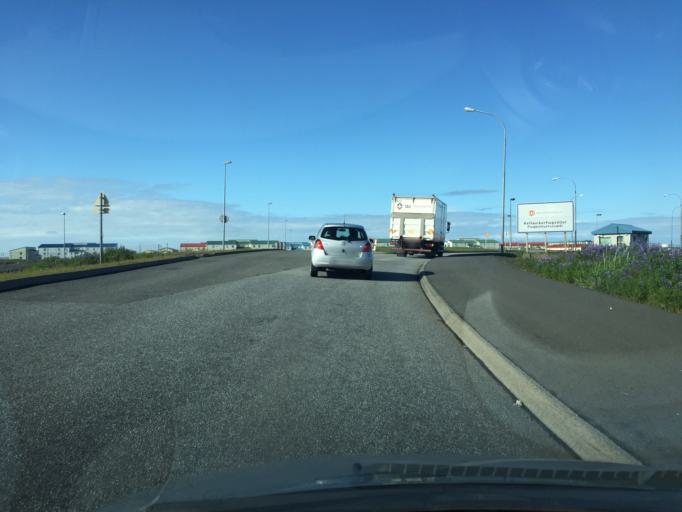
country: IS
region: Southern Peninsula
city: Reykjanesbaer
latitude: 63.9788
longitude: -22.5635
